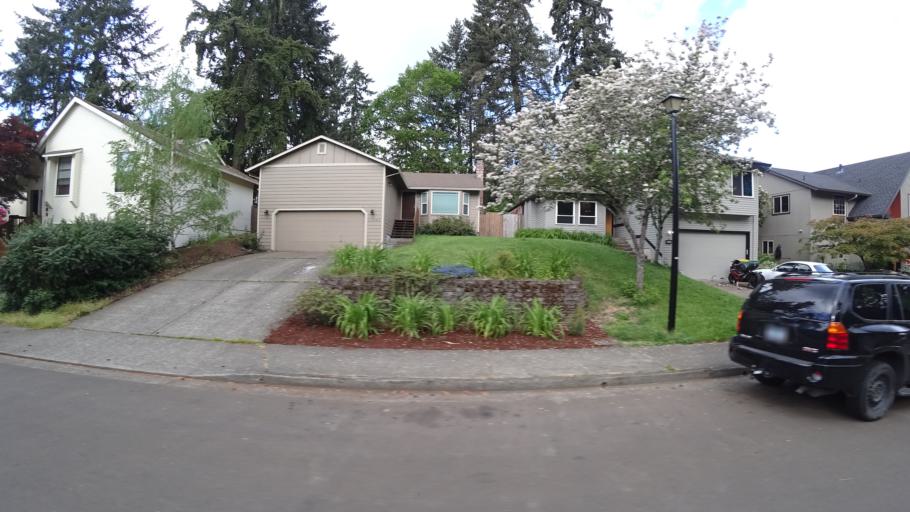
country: US
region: Oregon
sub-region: Washington County
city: Beaverton
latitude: 45.4709
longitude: -122.8322
